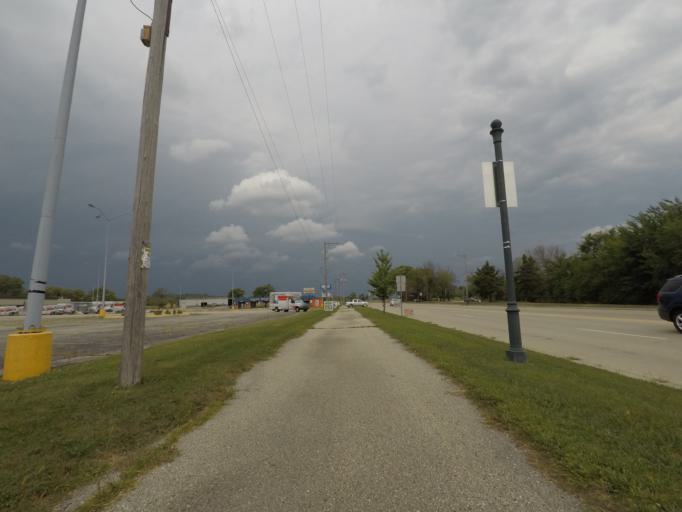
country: US
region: Wisconsin
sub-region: Jefferson County
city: Fort Atkinson
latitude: 42.9424
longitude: -88.8279
